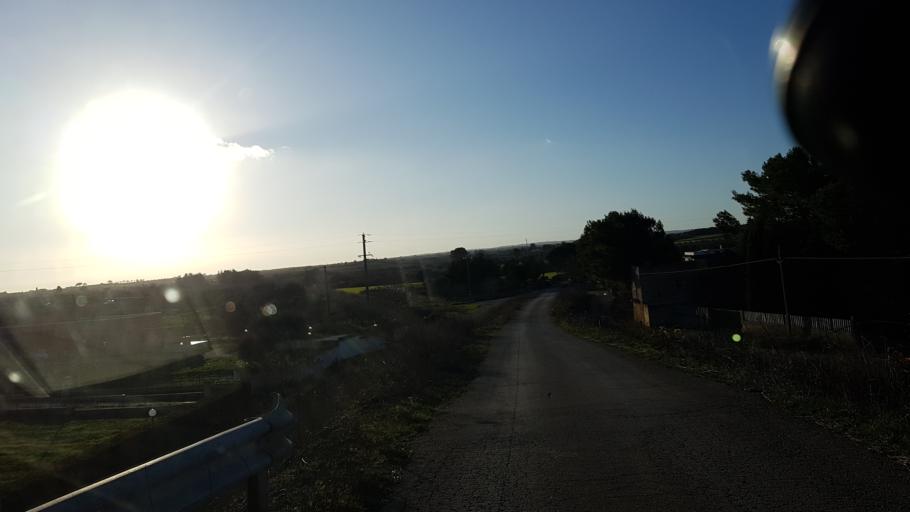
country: IT
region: Apulia
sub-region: Provincia di Bari
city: Gioia del Colle
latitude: 40.8007
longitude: 16.8988
